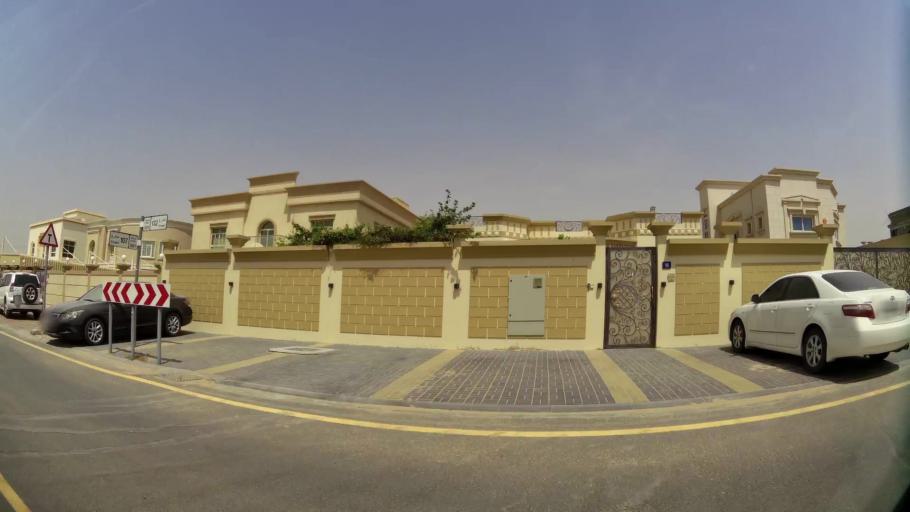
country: AE
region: Ash Shariqah
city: Sharjah
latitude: 25.2570
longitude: 55.4910
